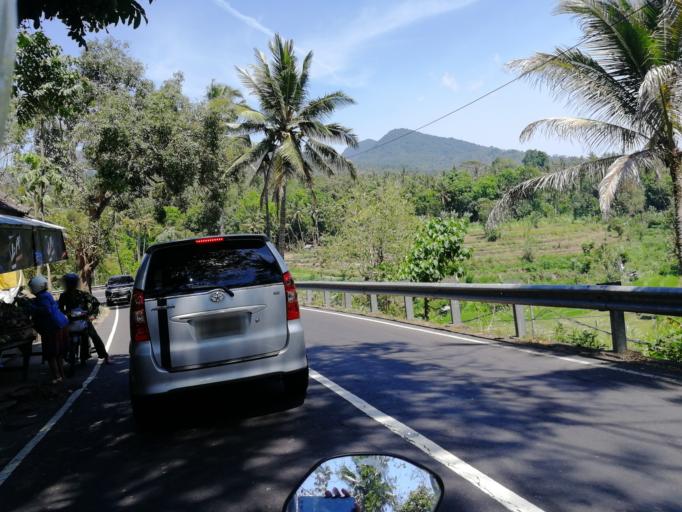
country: ID
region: Bali
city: Tistagede
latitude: -8.3745
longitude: 115.6086
